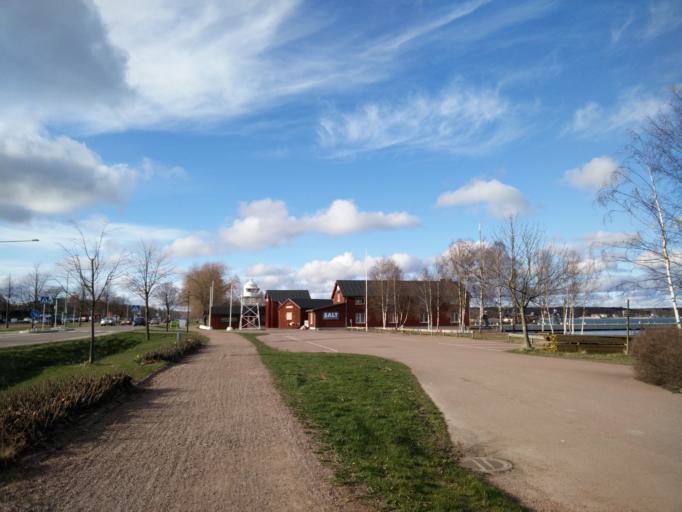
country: AX
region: Mariehamns stad
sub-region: Mariehamn
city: Mariehamn
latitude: 60.1040
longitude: 19.9449
